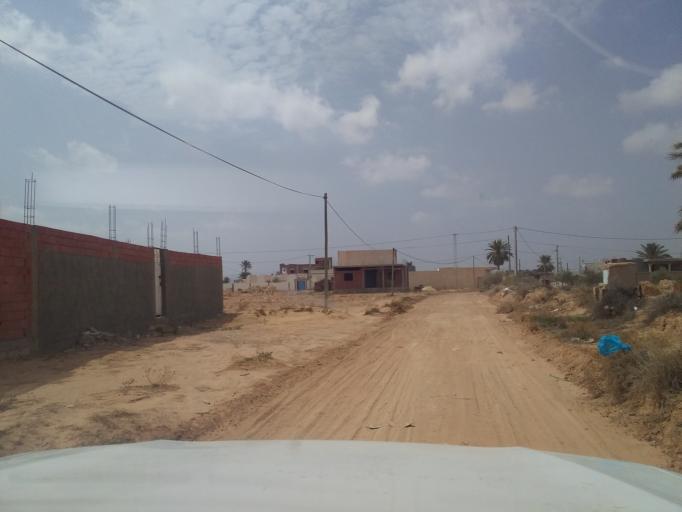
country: TN
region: Qabis
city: Matmata
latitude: 33.6207
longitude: 10.2674
